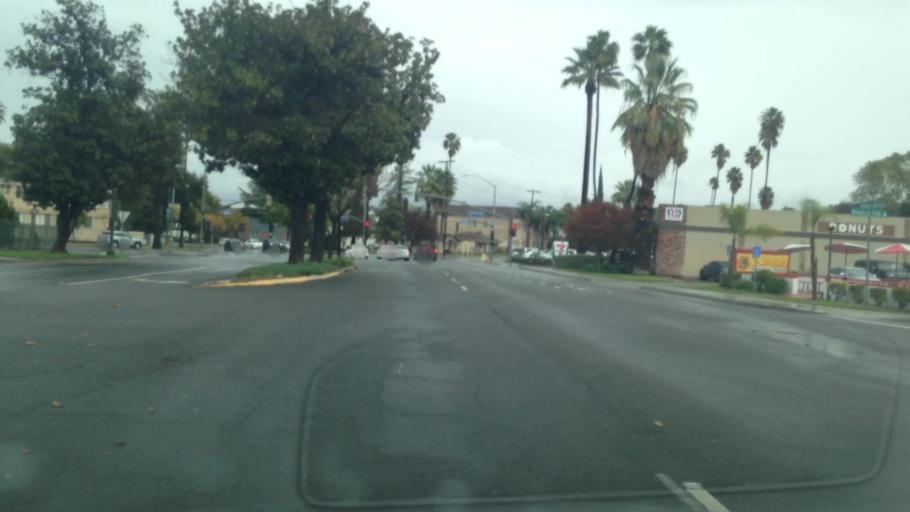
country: US
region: California
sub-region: Riverside County
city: Riverside
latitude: 33.9456
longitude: -117.4021
